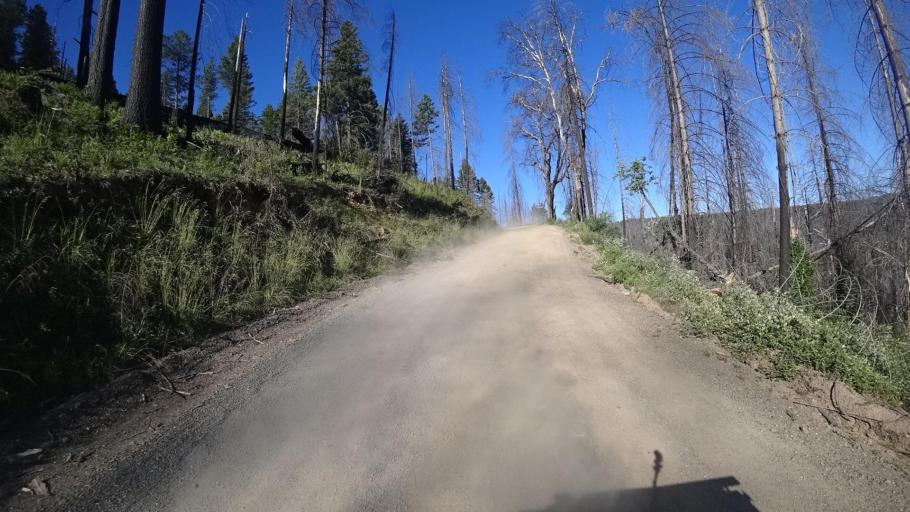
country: US
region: California
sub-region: Lake County
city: Upper Lake
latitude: 39.3782
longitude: -122.9895
